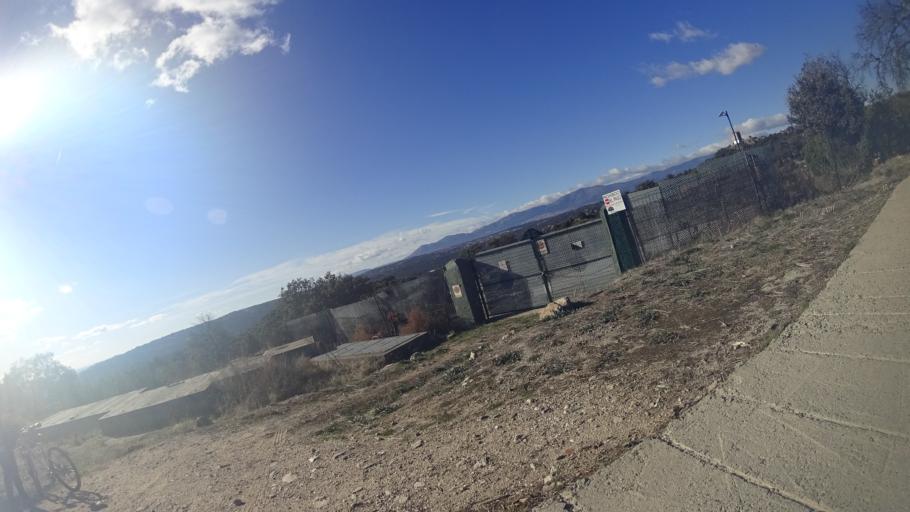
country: ES
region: Madrid
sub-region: Provincia de Madrid
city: Torrelodones
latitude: 40.5819
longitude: -3.9403
